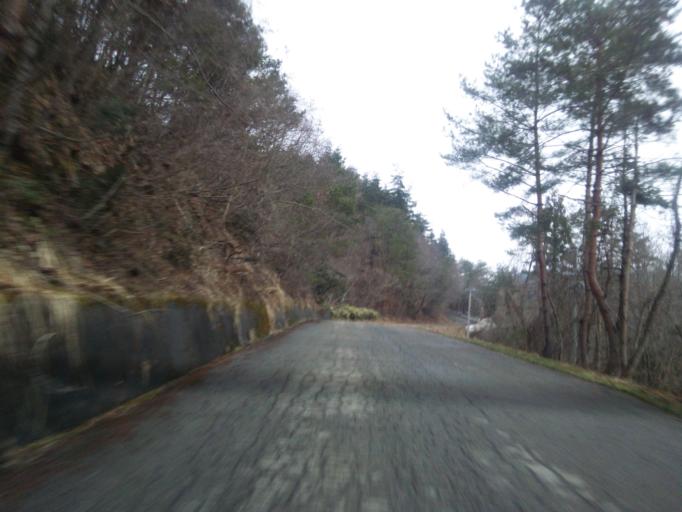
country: JP
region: Fukushima
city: Kitakata
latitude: 37.6810
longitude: 139.9238
